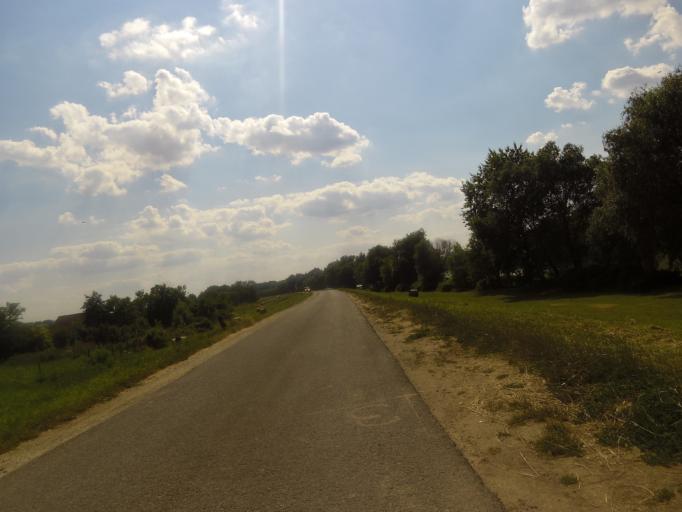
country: HU
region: Jasz-Nagykun-Szolnok
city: Tiszaszolos
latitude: 47.6061
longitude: 20.7173
